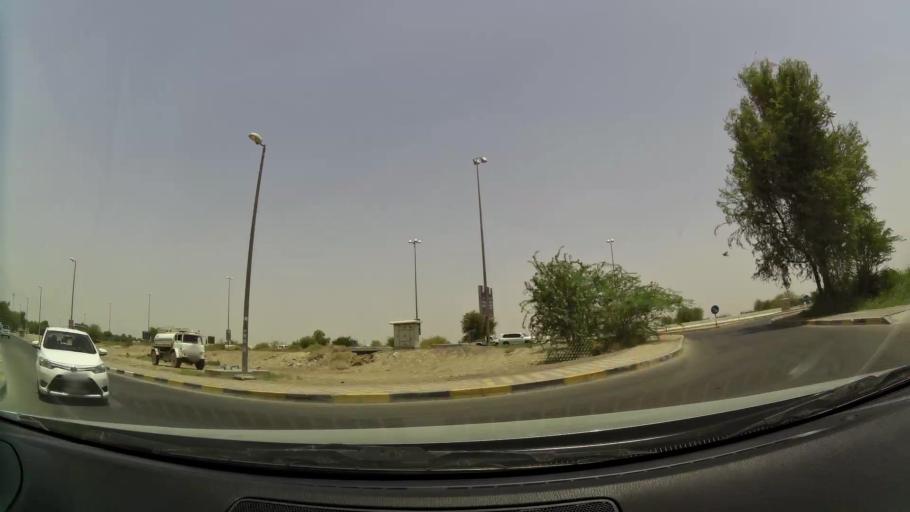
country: AE
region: Abu Dhabi
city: Al Ain
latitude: 24.2054
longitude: 55.7789
